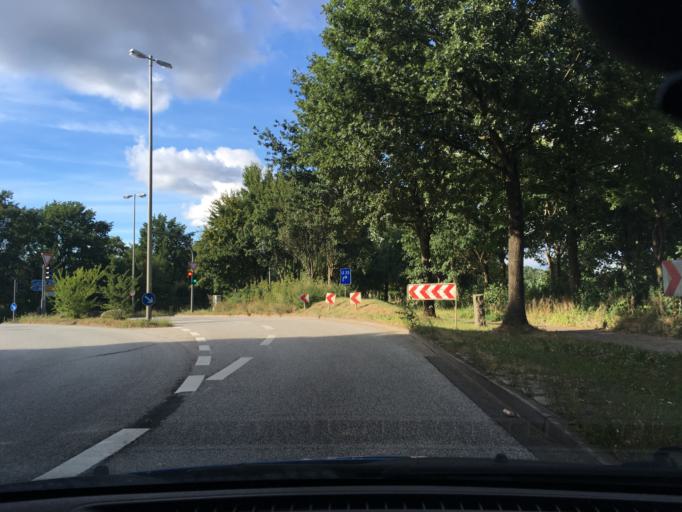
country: DE
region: Lower Saxony
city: Seevetal
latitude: 53.4285
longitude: 9.9316
